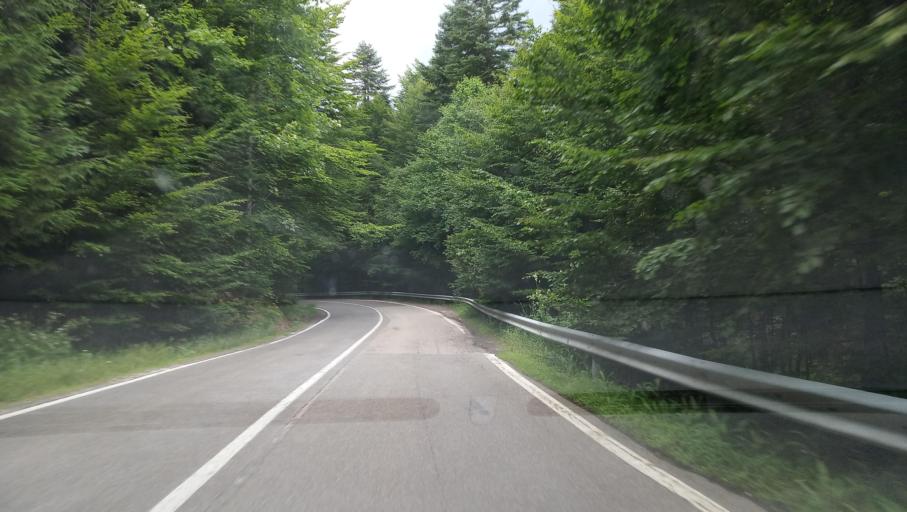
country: RO
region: Prahova
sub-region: Oras Sinaia
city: Sinaia
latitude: 45.3211
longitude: 25.5197
